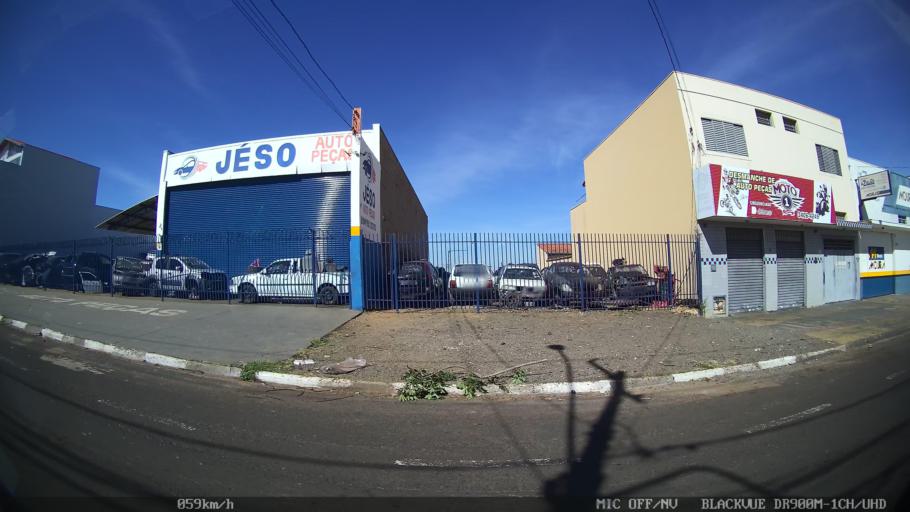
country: BR
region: Sao Paulo
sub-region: Franca
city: Franca
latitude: -20.5404
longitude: -47.3676
